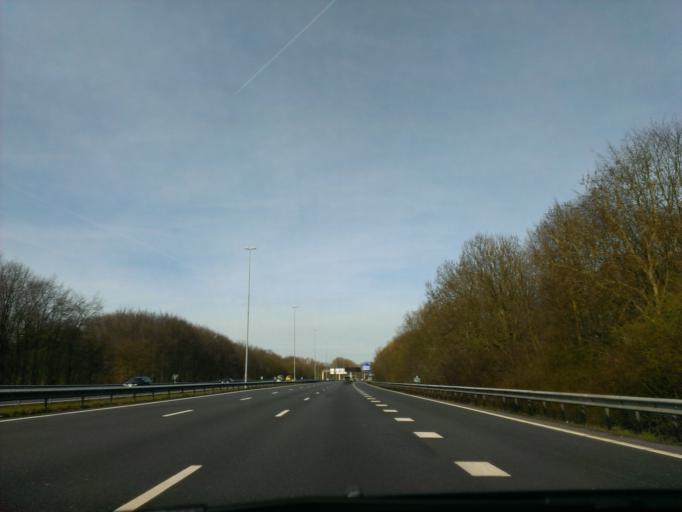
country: NL
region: North Holland
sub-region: Gemeente Amstelveen
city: Amstelveen
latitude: 52.3062
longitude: 4.8338
